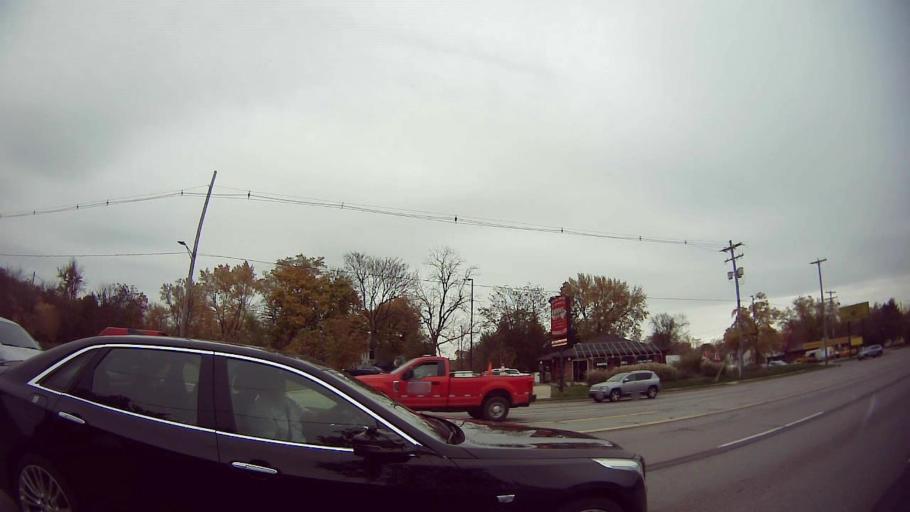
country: US
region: Michigan
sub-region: Oakland County
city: Sylvan Lake
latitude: 42.6281
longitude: -83.3255
